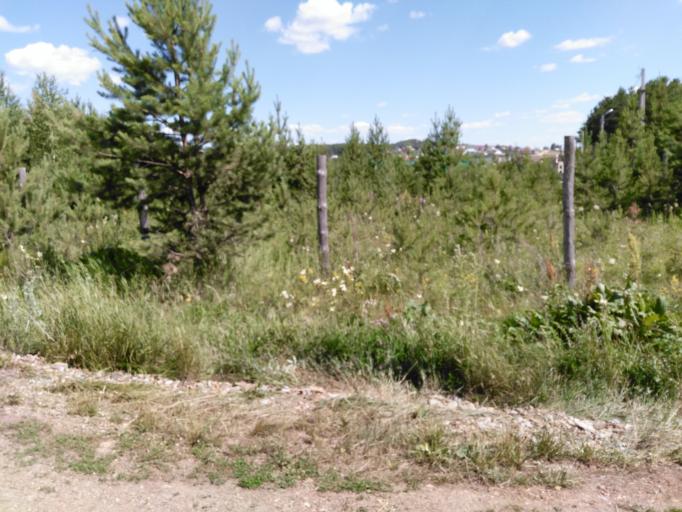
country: RU
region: Bashkortostan
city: Uchaly
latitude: 54.2878
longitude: 59.3558
